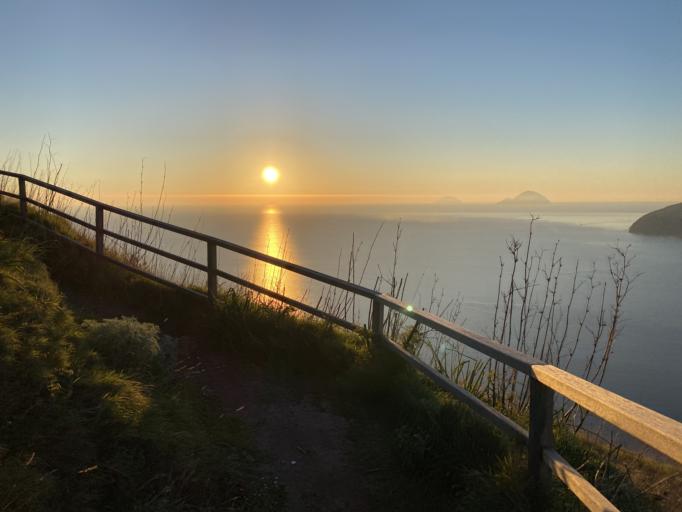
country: IT
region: Sicily
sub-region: Messina
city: Pianoconte
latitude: 38.5158
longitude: 14.9183
